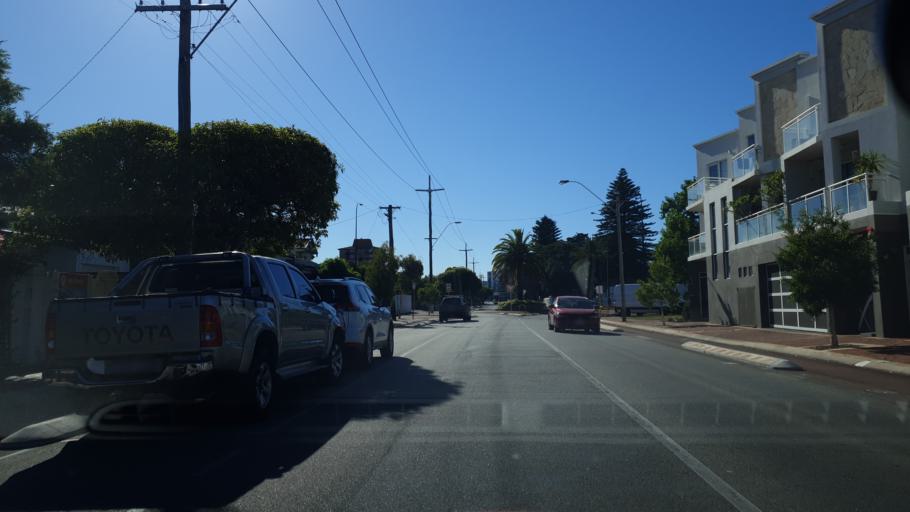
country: AU
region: Western Australia
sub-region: Vincent
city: Mount Lawley
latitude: -31.9434
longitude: 115.8688
